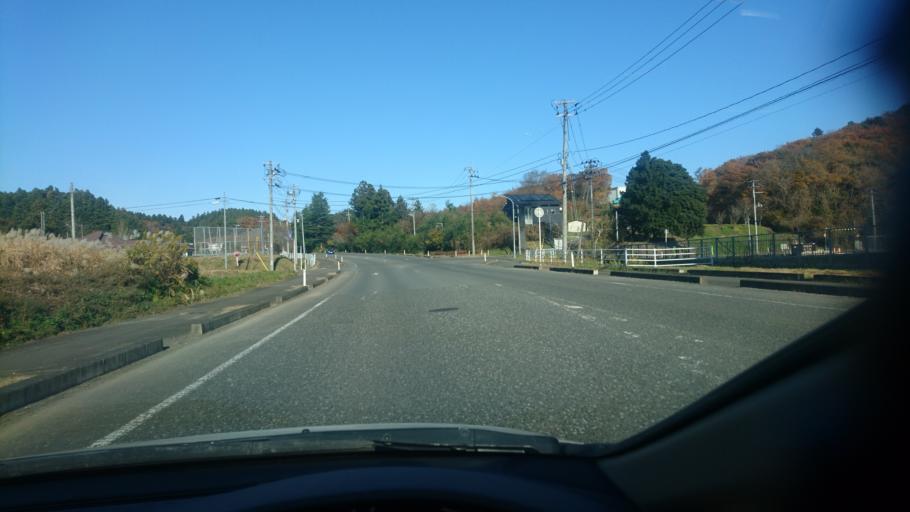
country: JP
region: Miyagi
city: Tomiya
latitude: 38.4518
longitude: 140.8914
